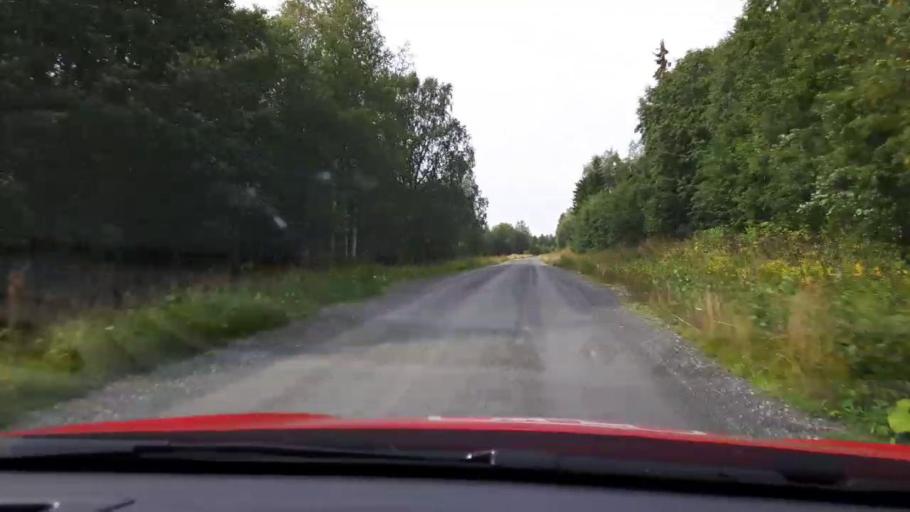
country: SE
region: Jaemtland
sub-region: Are Kommun
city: Are
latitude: 63.7442
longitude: 12.9830
